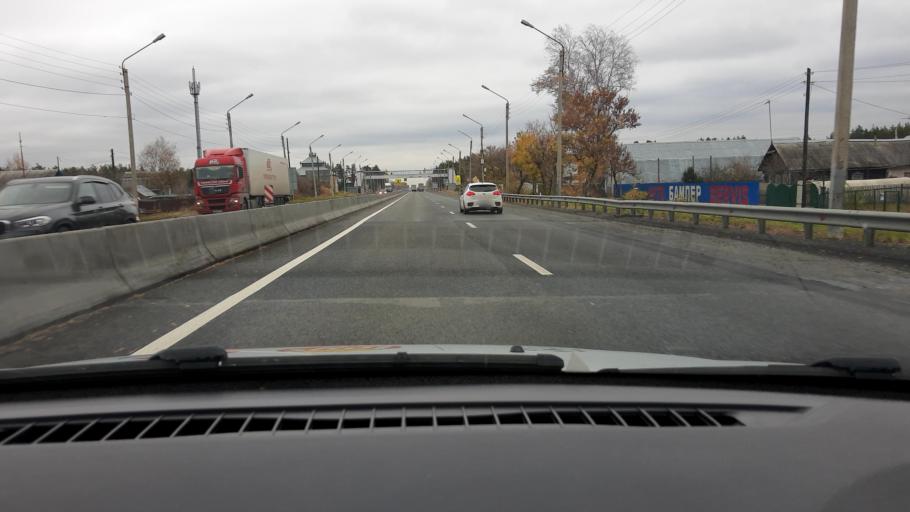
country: RU
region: Nizjnij Novgorod
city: Babino
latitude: 56.3023
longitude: 43.5711
